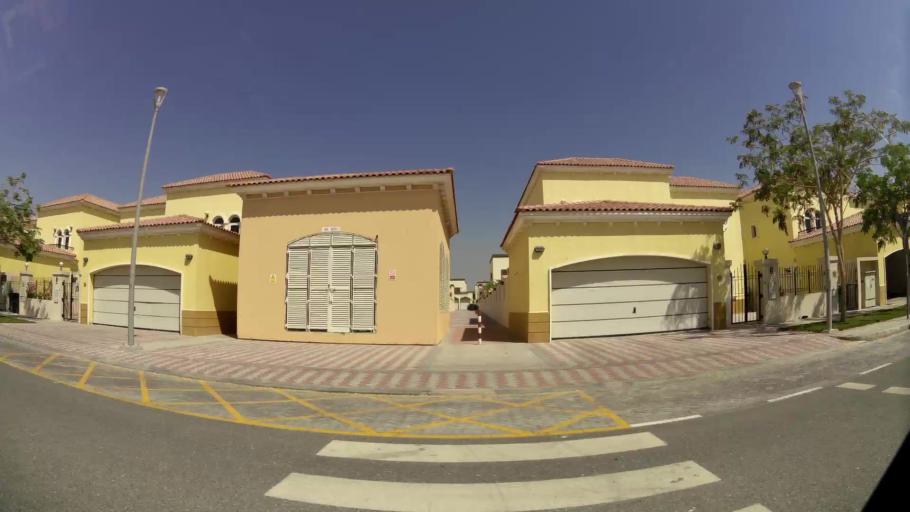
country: AE
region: Dubai
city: Dubai
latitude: 25.0475
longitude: 55.1518
